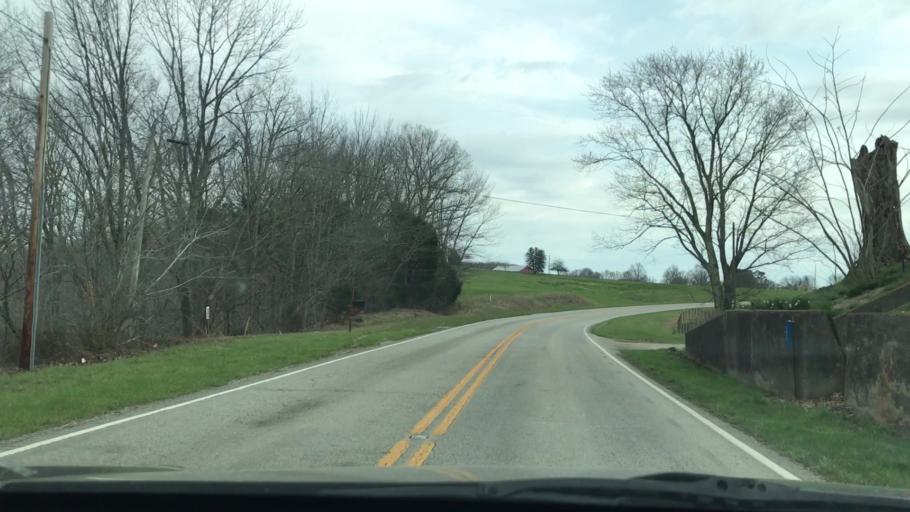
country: US
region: Kentucky
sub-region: Hart County
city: Munfordville
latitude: 37.2996
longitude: -85.7634
